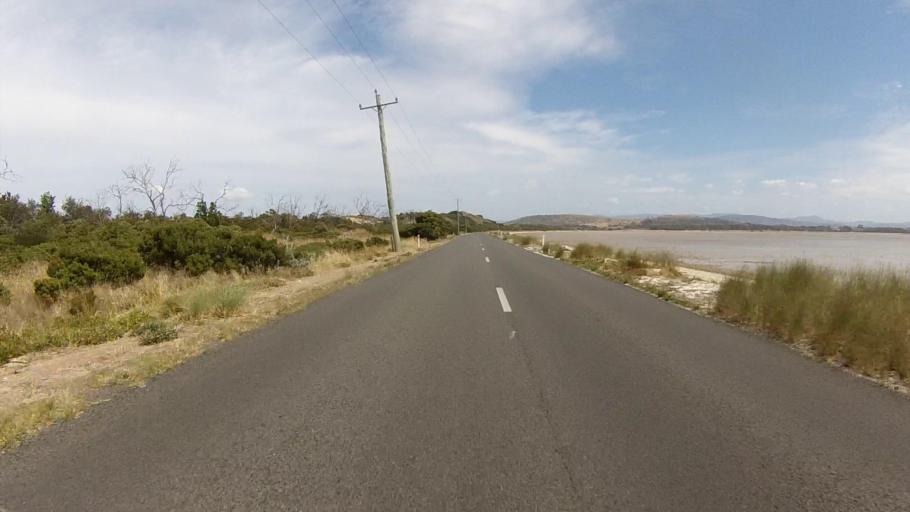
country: AU
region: Tasmania
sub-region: Clarence
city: Sandford
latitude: -43.0296
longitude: 147.4639
